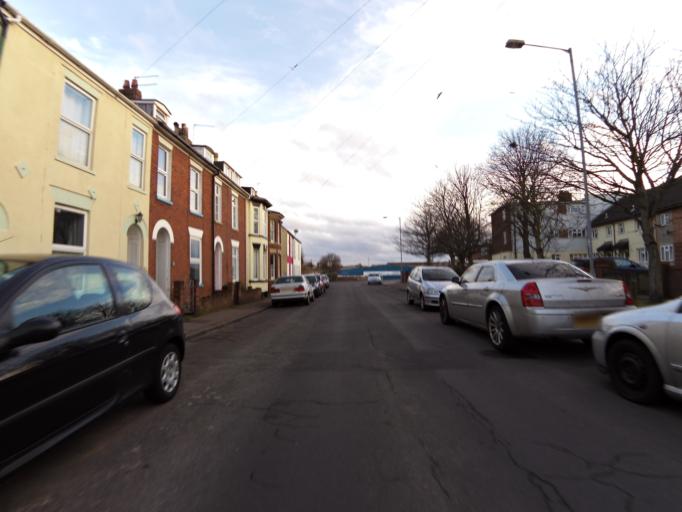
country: GB
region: England
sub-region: Norfolk
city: Great Yarmouth
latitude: 52.6012
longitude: 1.7297
